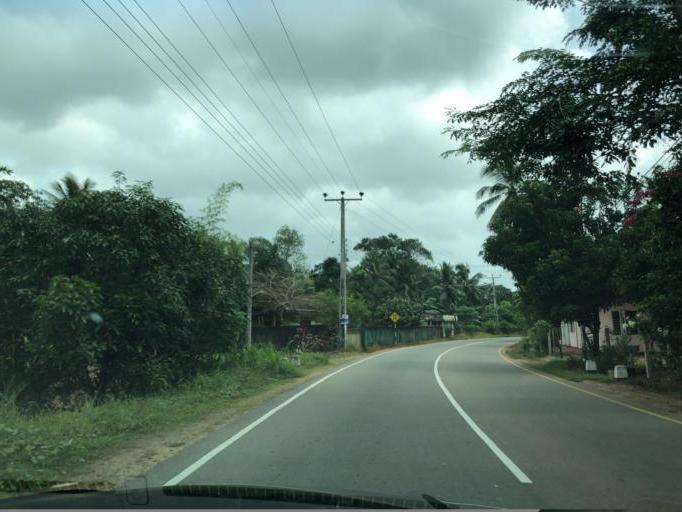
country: LK
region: Western
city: Horana South
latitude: 6.6852
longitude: 80.1385
